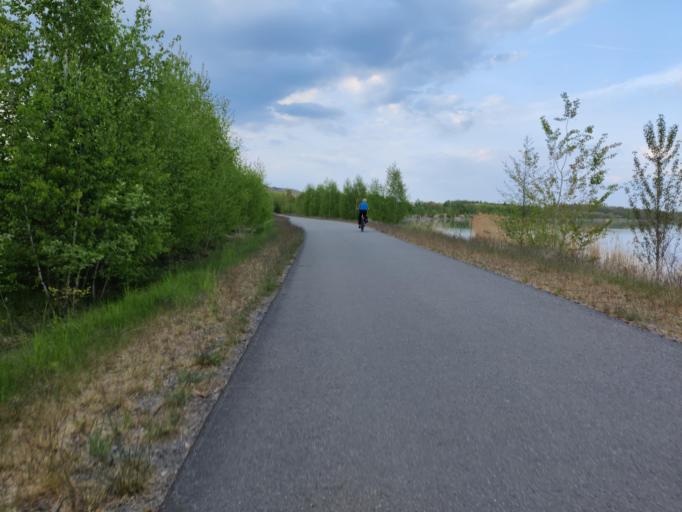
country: DE
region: Saxony
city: Rotha
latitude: 51.2305
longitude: 12.4273
